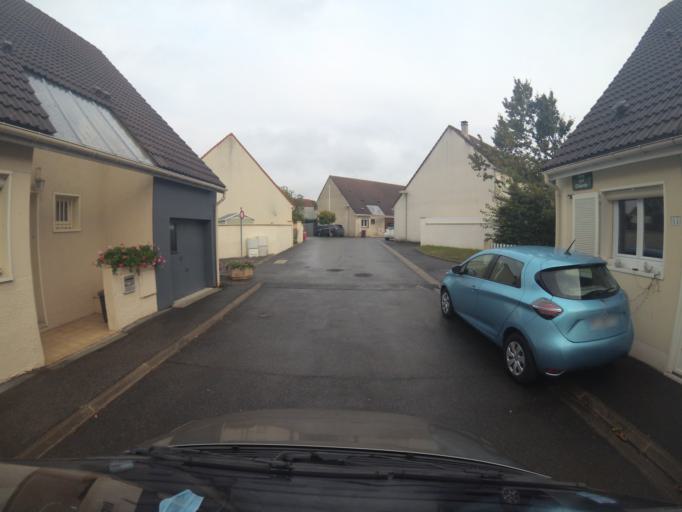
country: FR
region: Ile-de-France
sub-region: Departement de Seine-et-Marne
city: Chanteloup-en-Brie
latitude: 48.8579
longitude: 2.7331
